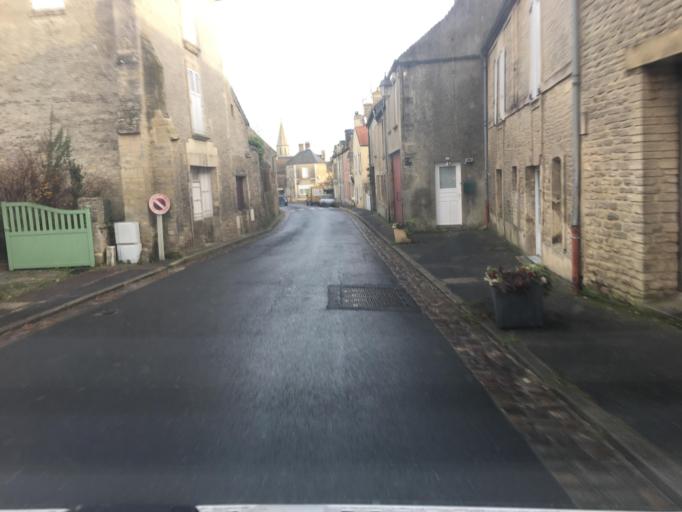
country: FR
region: Lower Normandy
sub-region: Departement du Calvados
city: Creully
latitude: 49.2831
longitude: -0.5421
